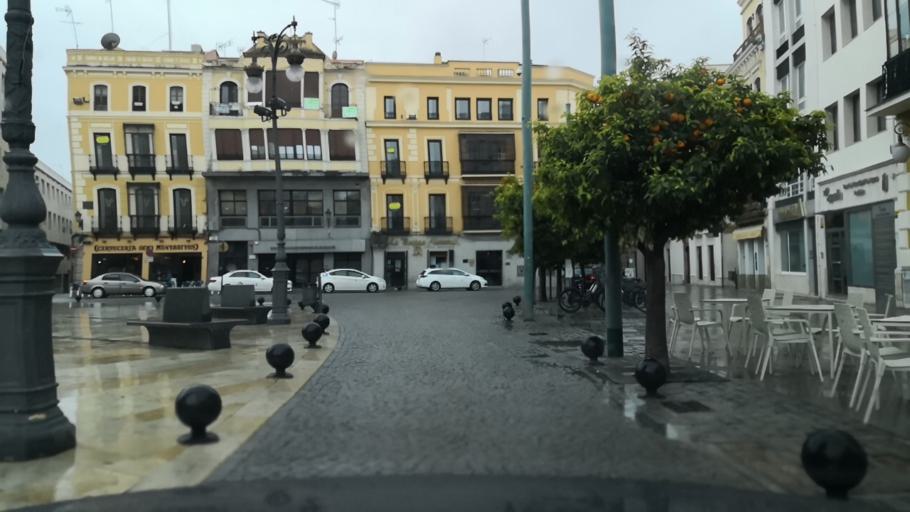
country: ES
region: Extremadura
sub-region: Provincia de Badajoz
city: Badajoz
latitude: 38.8785
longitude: -6.9702
